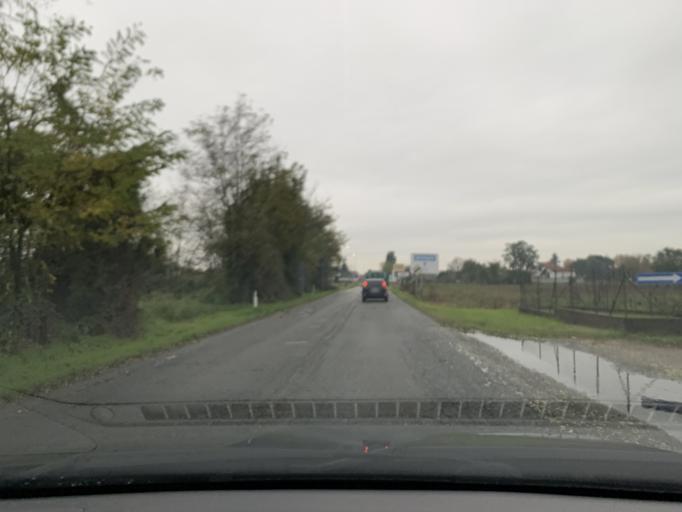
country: IT
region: Lombardy
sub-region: Provincia di Como
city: Rovello Porro
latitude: 45.6450
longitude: 9.0495
